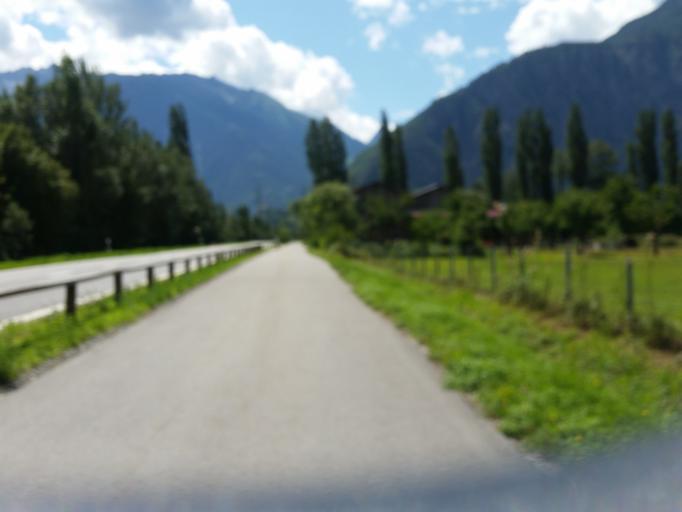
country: CH
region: Valais
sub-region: Martigny District
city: Martigny-Ville
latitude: 46.1212
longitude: 7.0841
